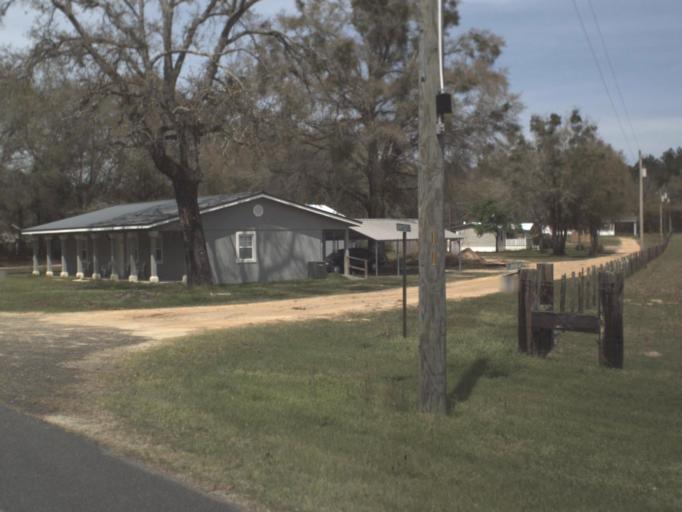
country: US
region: Florida
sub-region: Walton County
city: DeFuniak Springs
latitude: 30.7343
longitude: -85.9487
